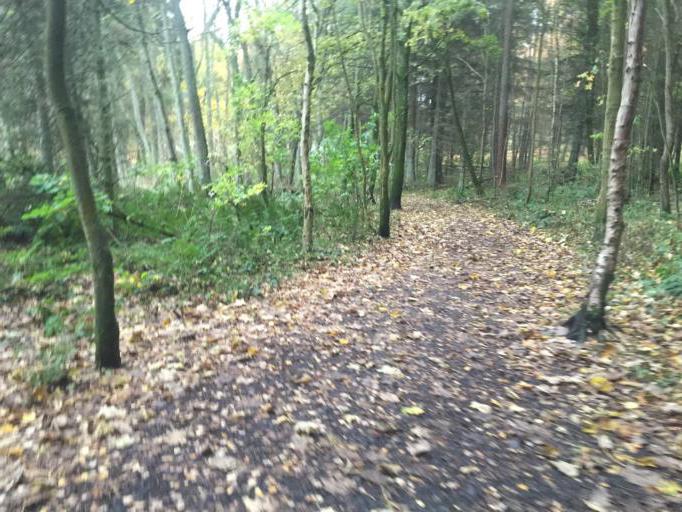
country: GB
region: Scotland
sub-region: West Lothian
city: Linlithgow
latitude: 55.9514
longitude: -3.5896
